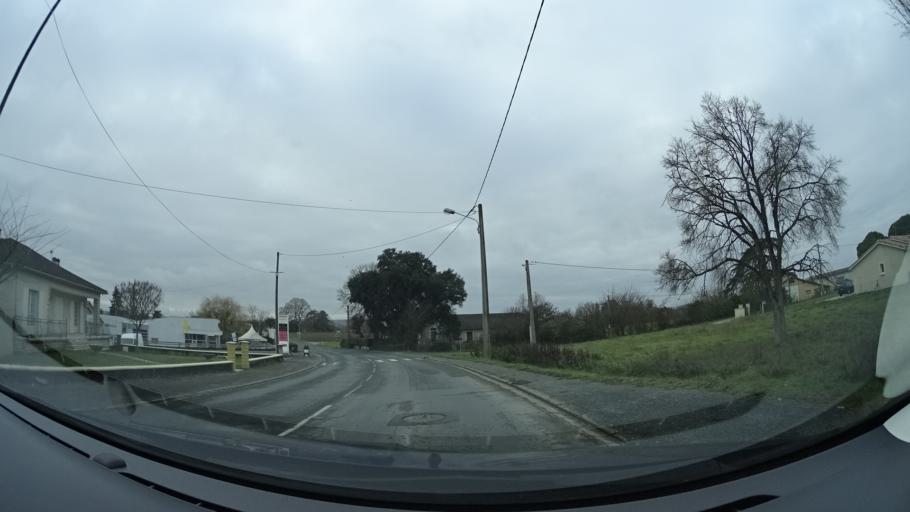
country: FR
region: Aquitaine
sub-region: Departement du Lot-et-Garonne
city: Monflanquin
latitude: 44.5296
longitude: 0.7645
